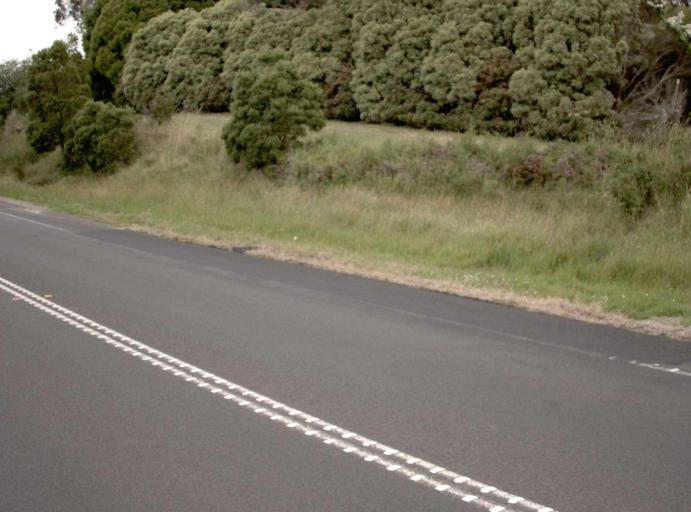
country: AU
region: Victoria
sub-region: Baw Baw
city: Warragul
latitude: -38.4486
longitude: 145.8806
